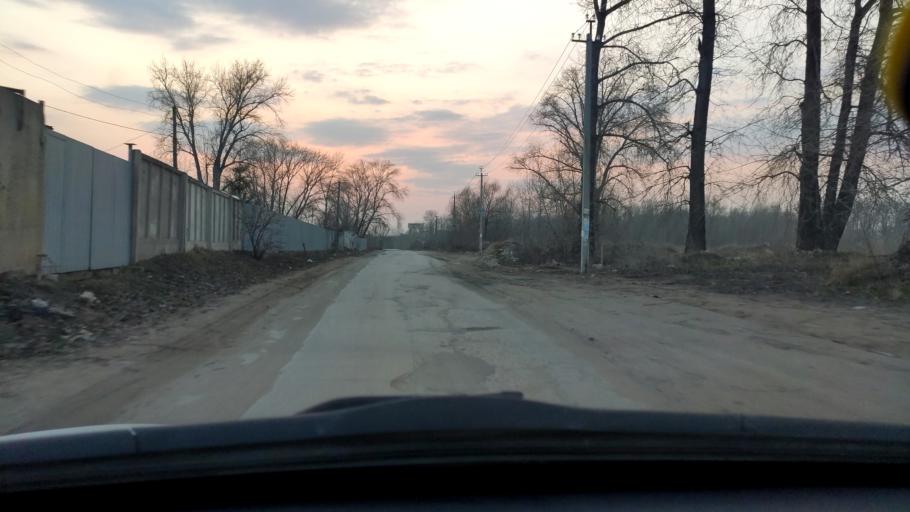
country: RU
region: Samara
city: Zhigulevsk
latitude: 53.4570
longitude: 49.5170
